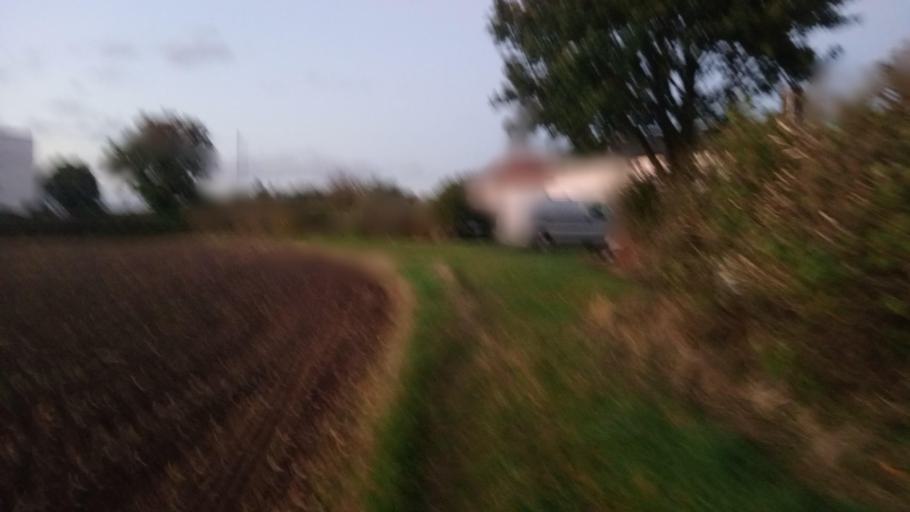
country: GB
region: England
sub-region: Cambridgeshire
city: Linton
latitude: 52.0576
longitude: 0.3256
